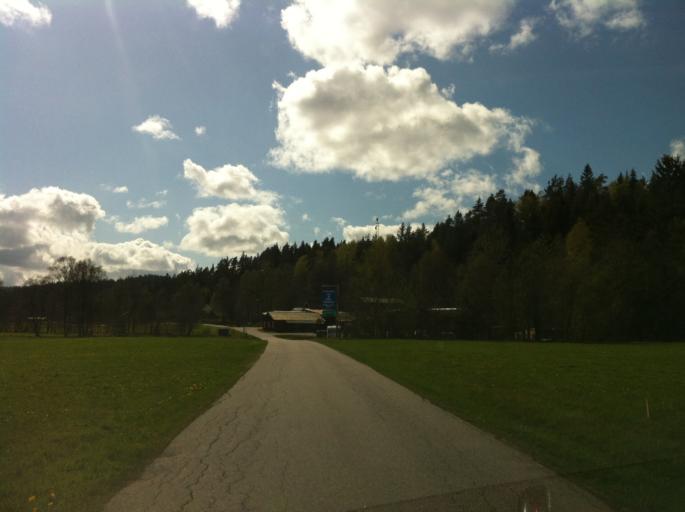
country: SE
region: Vaestra Goetaland
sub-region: Bollebygds Kommun
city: Bollebygd
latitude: 57.7943
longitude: 12.6284
